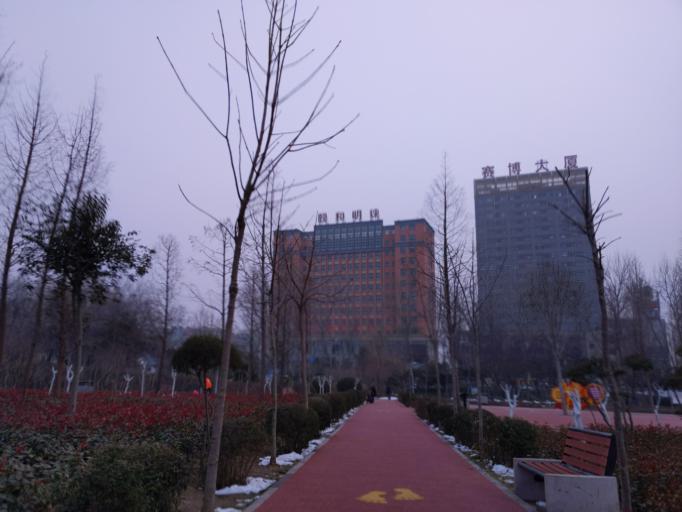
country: CN
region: Henan Sheng
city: Puyang
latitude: 35.7780
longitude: 115.0270
